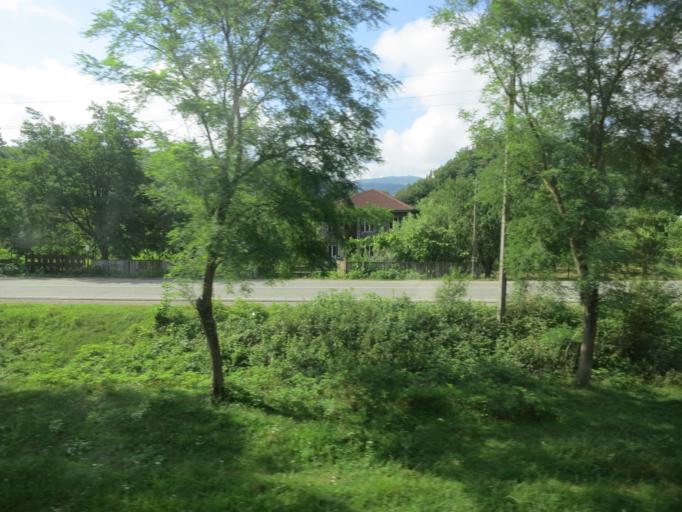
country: GE
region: Imereti
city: Samtredia
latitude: 42.1051
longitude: 42.3035
